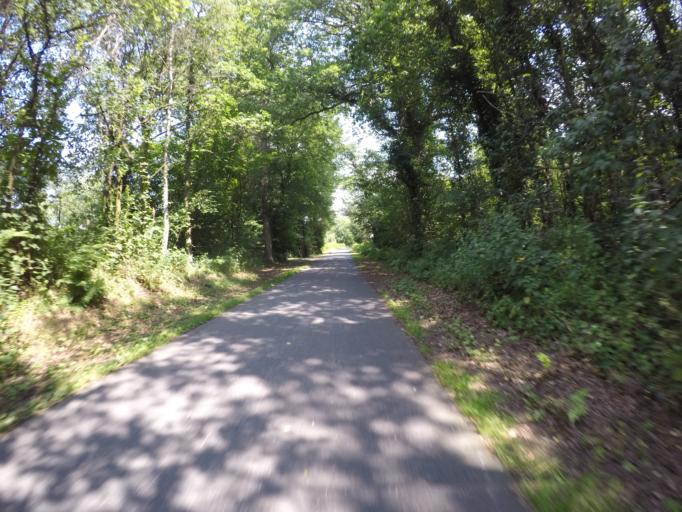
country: DE
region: North Rhine-Westphalia
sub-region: Regierungsbezirk Munster
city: Rhede
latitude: 51.8233
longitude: 6.7508
